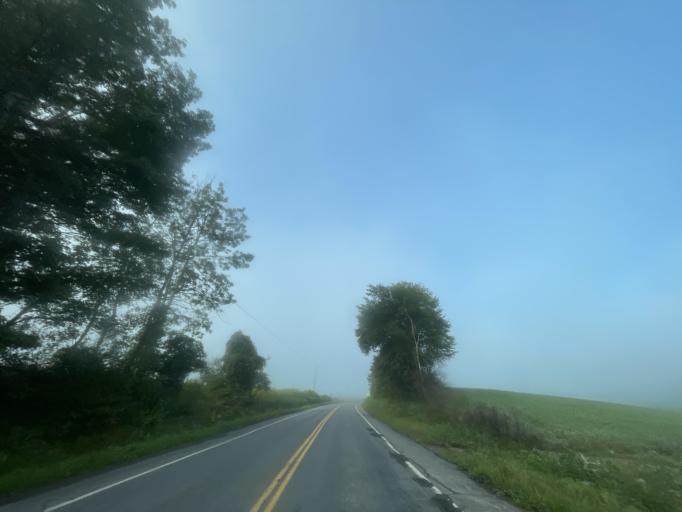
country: US
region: New York
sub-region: Chenango County
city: Greene
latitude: 42.3635
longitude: -75.6701
